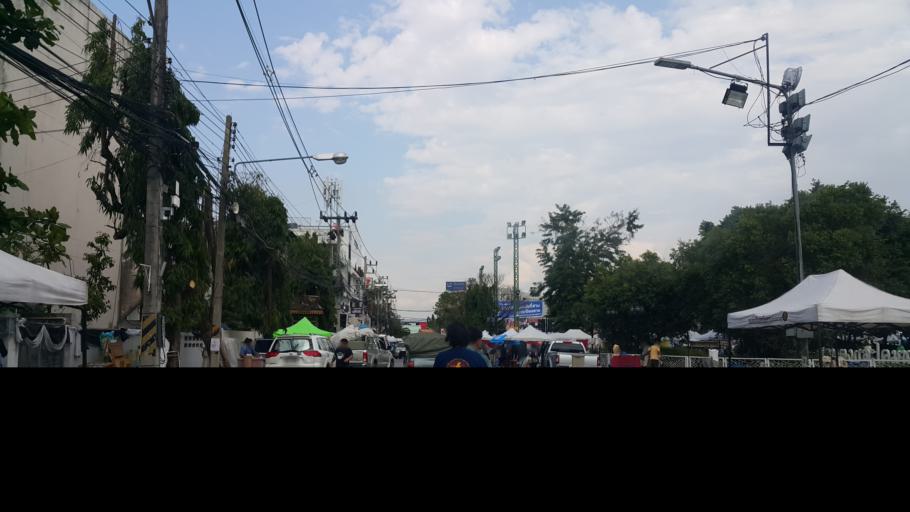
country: TH
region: Chiang Rai
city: Chiang Rai
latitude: 19.9241
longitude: 99.8449
